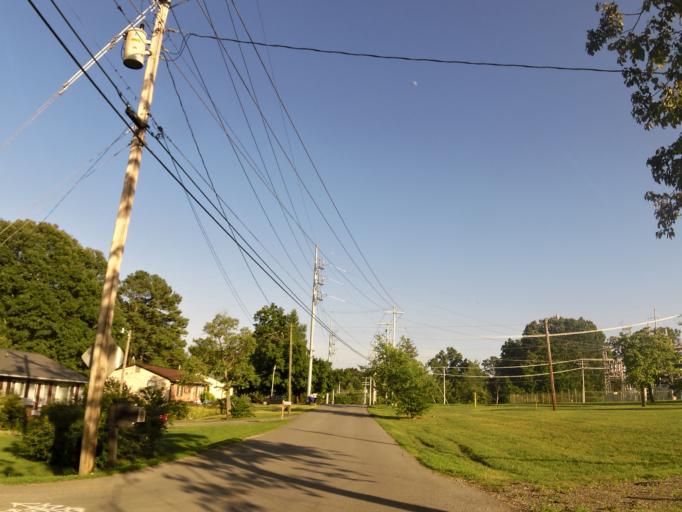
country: US
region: Tennessee
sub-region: Knox County
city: Knoxville
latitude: 35.9173
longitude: -83.9371
